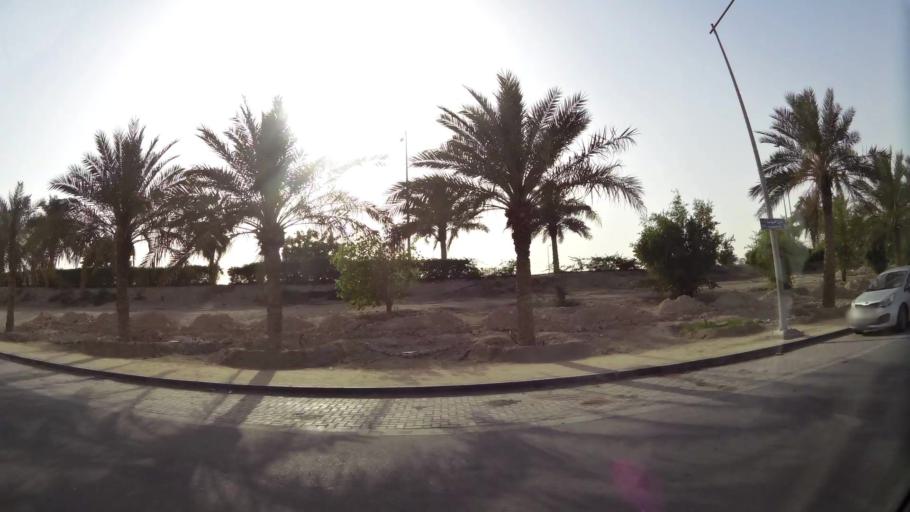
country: QA
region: Baladiyat ar Rayyan
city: Ar Rayyan
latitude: 25.2277
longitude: 51.4319
